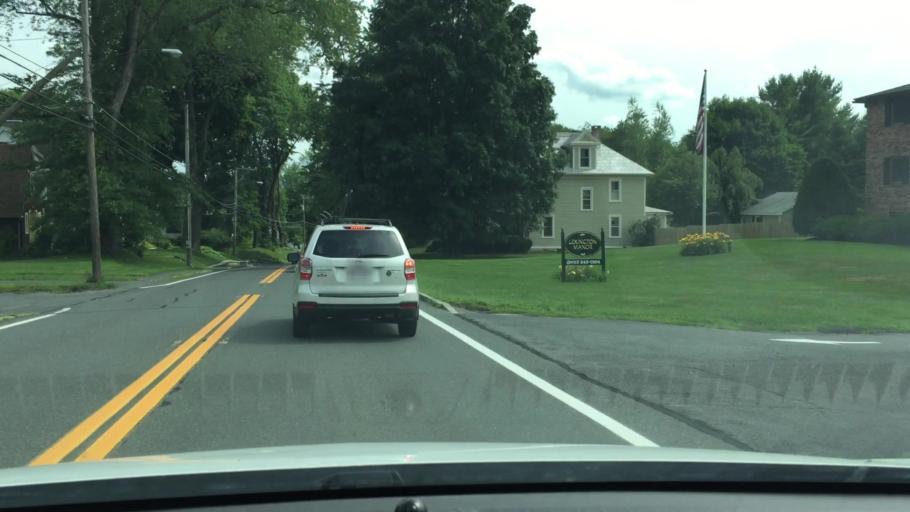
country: US
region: Massachusetts
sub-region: Berkshire County
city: Lee
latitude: 42.3136
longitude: -73.2556
